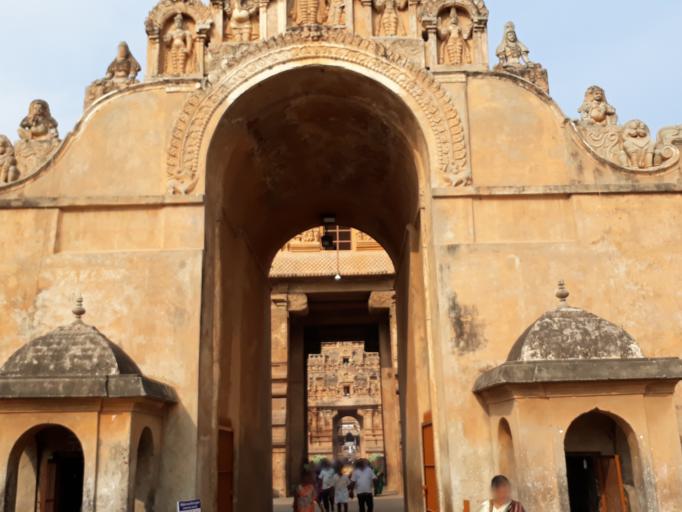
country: IN
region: Tamil Nadu
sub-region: Thanjavur
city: Thanjavur
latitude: 10.7834
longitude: 79.1337
